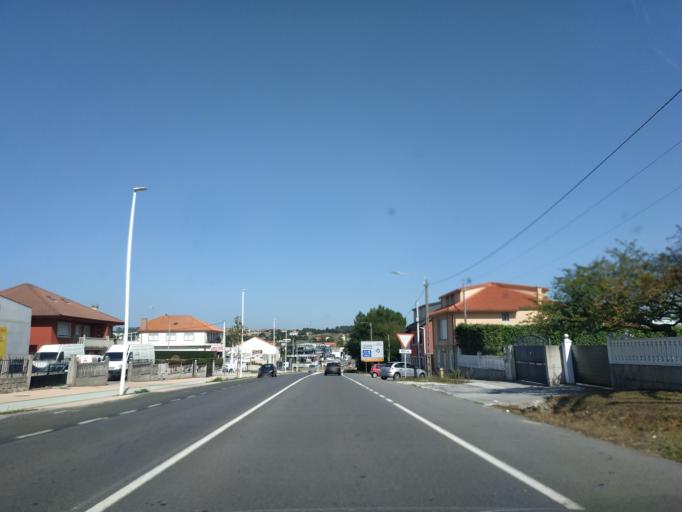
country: ES
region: Galicia
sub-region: Provincia da Coruna
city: Carballo
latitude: 43.2269
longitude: -8.6775
